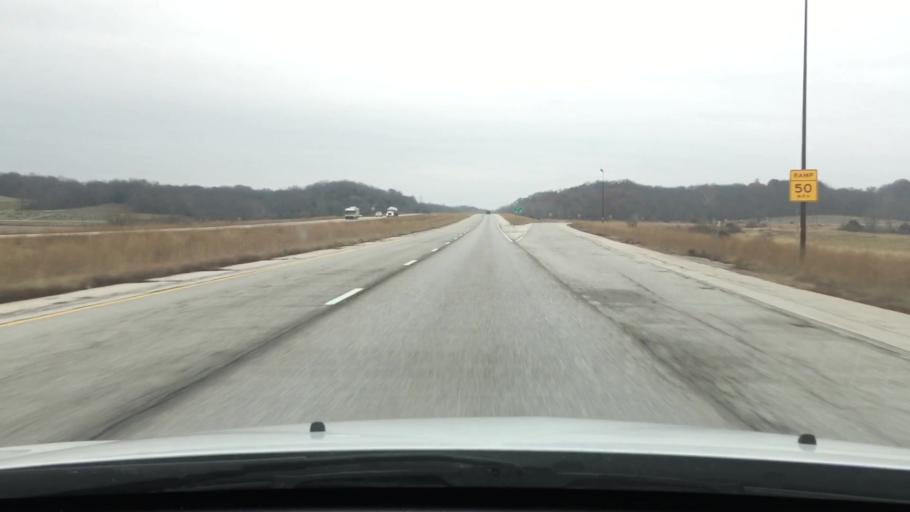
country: US
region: Illinois
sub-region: Scott County
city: Winchester
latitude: 39.6850
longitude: -90.5783
